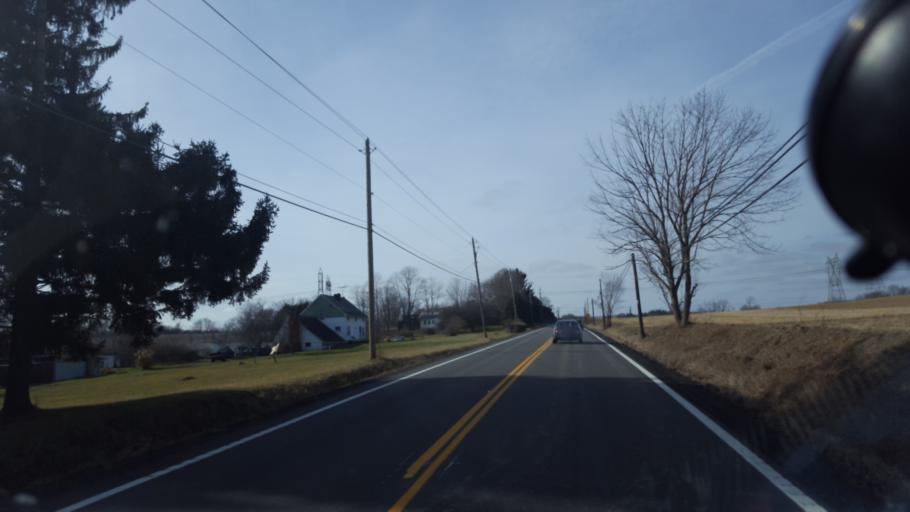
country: US
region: Ohio
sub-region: Columbiana County
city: Lisbon
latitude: 40.7700
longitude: -80.7990
